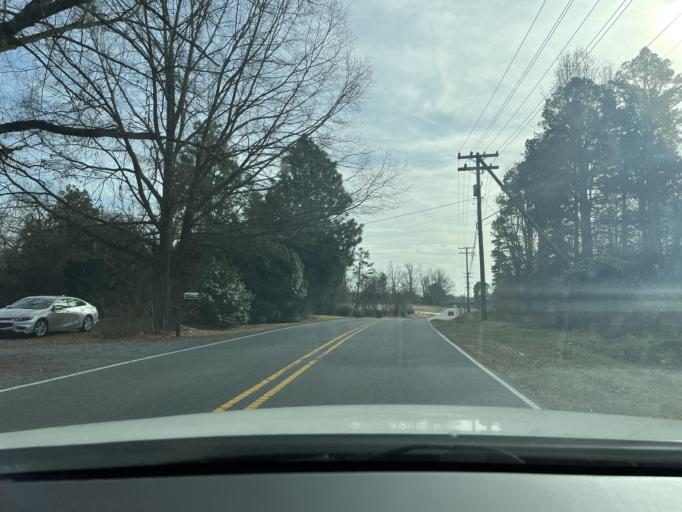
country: US
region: North Carolina
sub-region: Guilford County
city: Pleasant Garden
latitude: 36.0037
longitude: -79.7775
